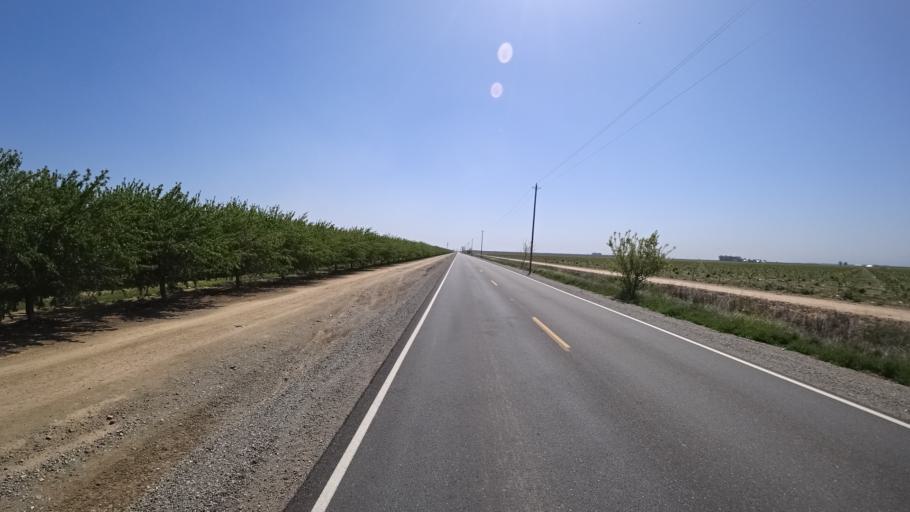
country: US
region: California
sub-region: Glenn County
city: Willows
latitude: 39.6223
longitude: -122.1376
